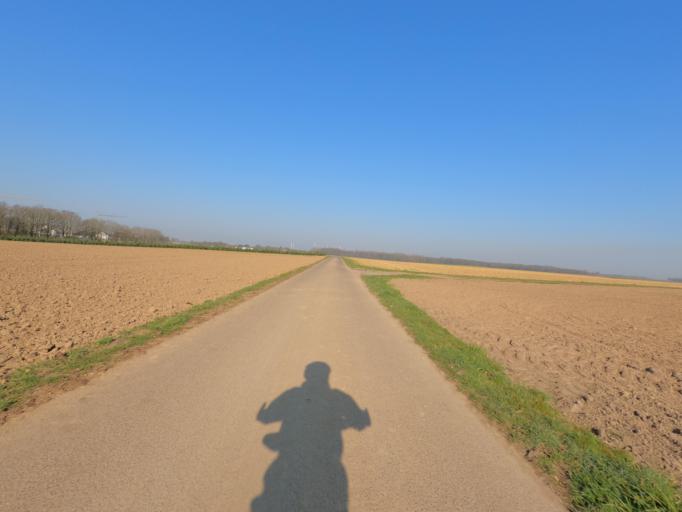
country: DE
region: North Rhine-Westphalia
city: Wegberg
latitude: 51.1053
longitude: 6.2816
